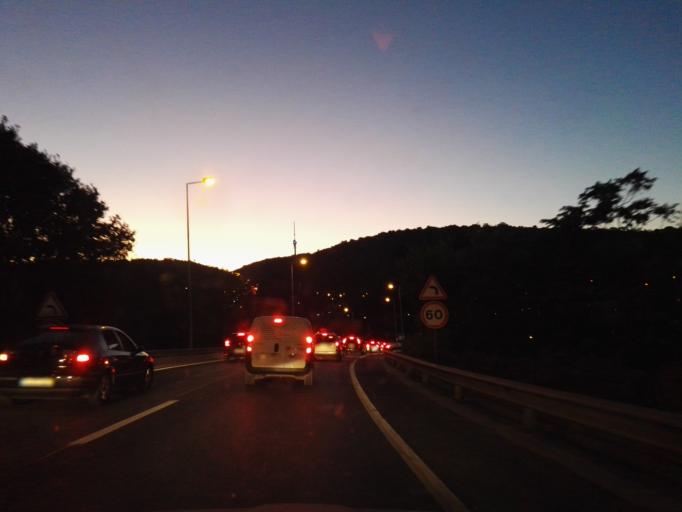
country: PT
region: Lisbon
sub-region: Lisbon
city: Lisbon
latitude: 38.7227
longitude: -9.1717
